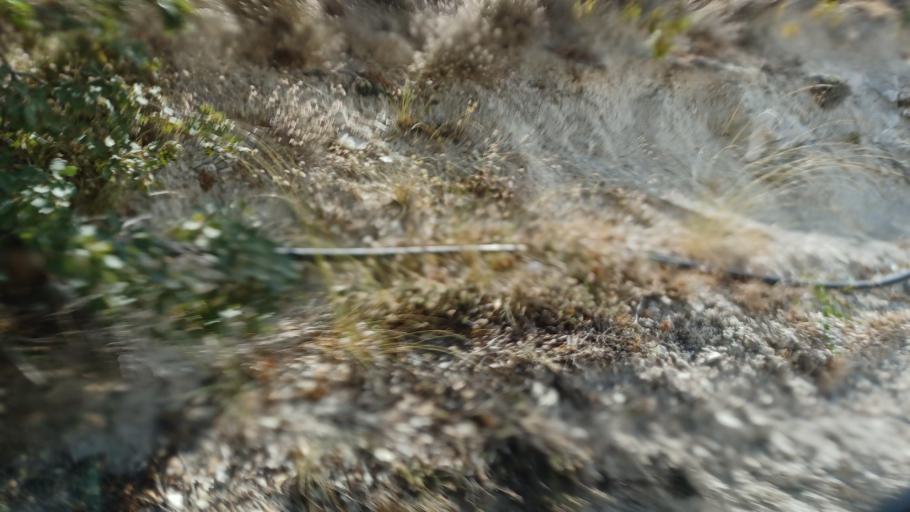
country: CY
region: Pafos
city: Mesogi
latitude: 34.8799
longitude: 32.6103
